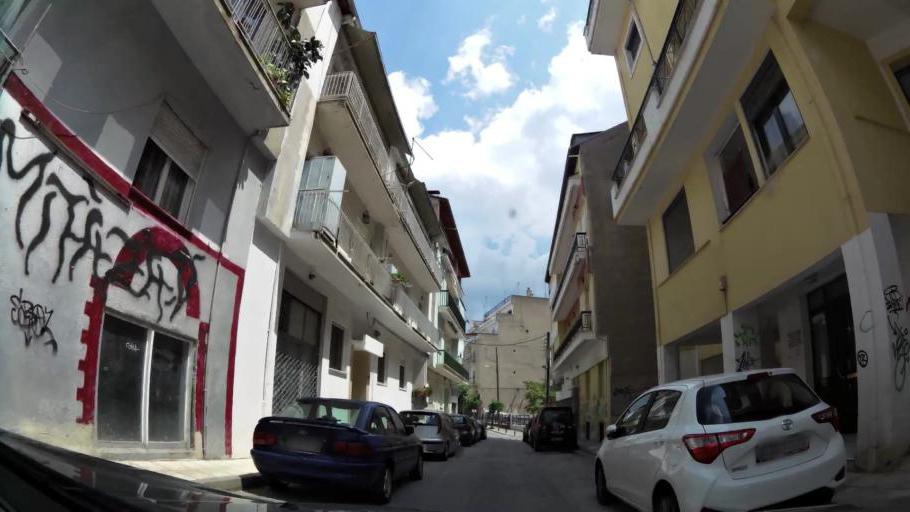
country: GR
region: West Macedonia
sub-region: Nomos Kozanis
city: Kozani
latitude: 40.3029
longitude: 21.7867
